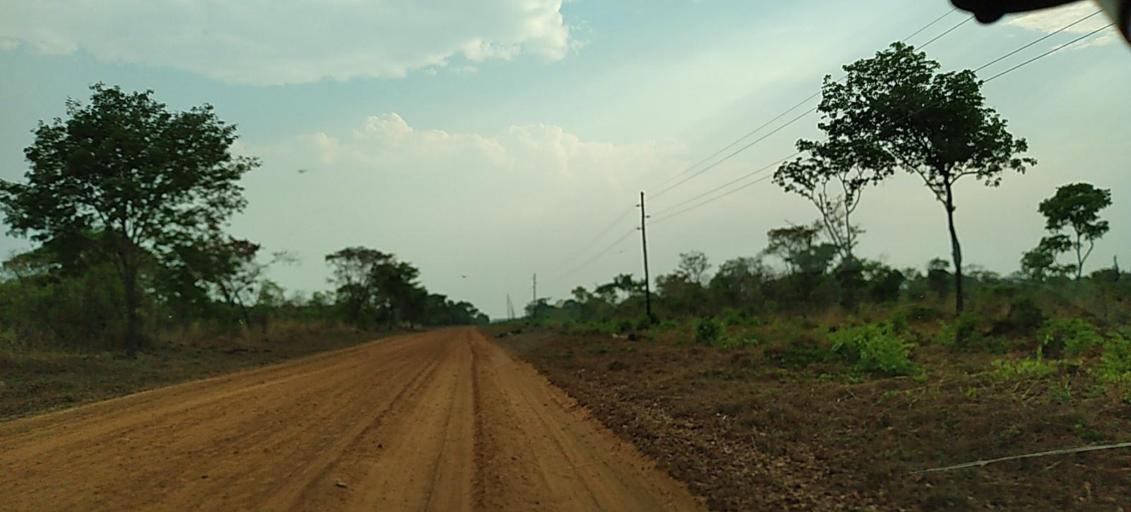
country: ZM
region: North-Western
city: Kabompo
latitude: -13.8993
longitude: 23.6563
